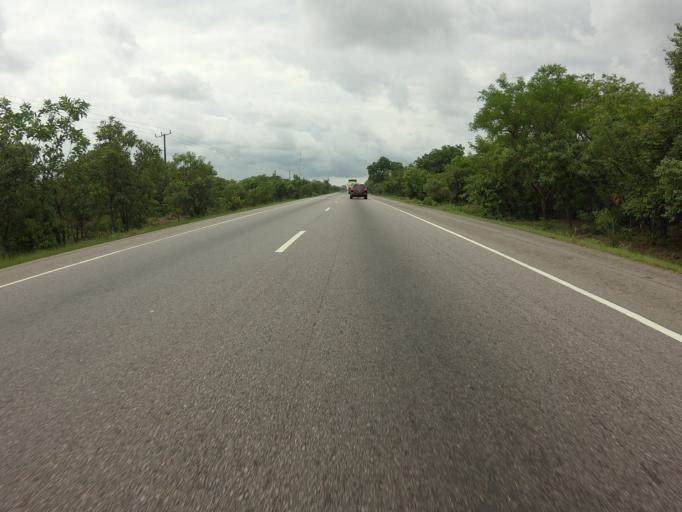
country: GH
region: Northern
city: Tamale
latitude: 9.0560
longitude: -1.3147
